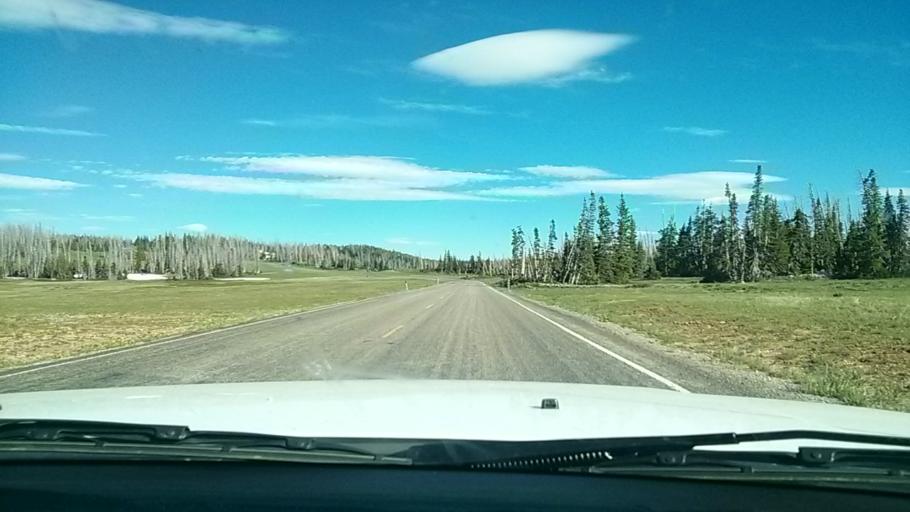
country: US
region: Utah
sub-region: Iron County
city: Parowan
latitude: 37.6608
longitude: -112.8375
